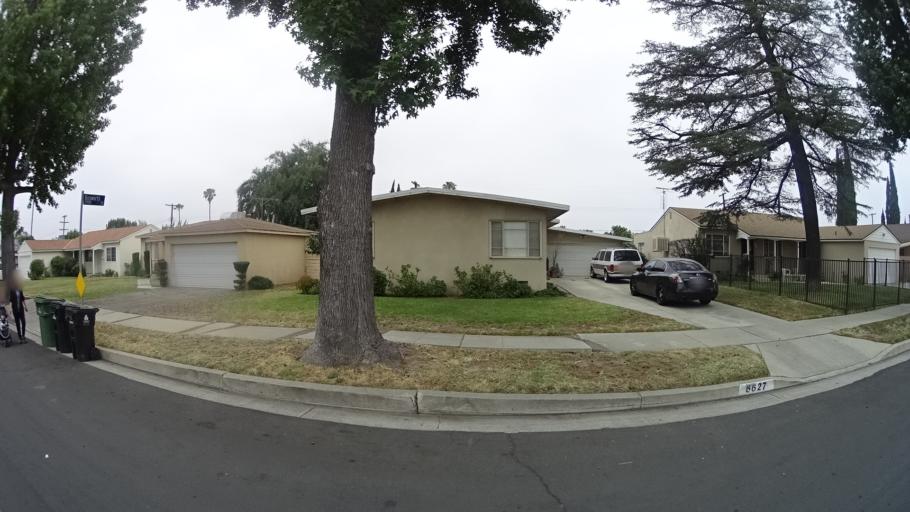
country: US
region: California
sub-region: Los Angeles County
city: Van Nuys
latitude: 34.1912
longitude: -118.4167
